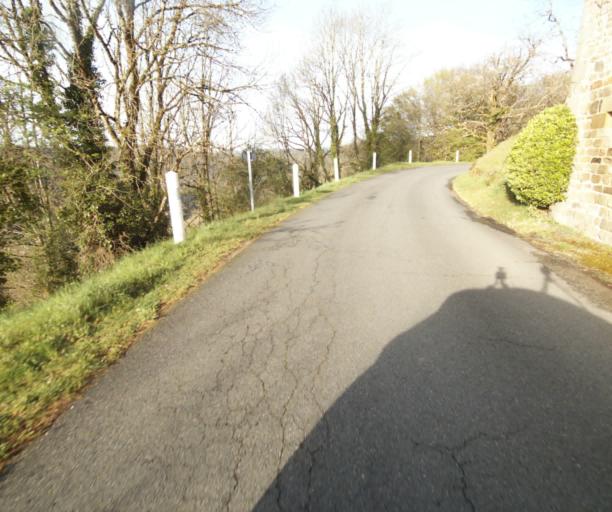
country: FR
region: Limousin
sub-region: Departement de la Correze
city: Correze
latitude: 45.3000
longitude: 1.8466
